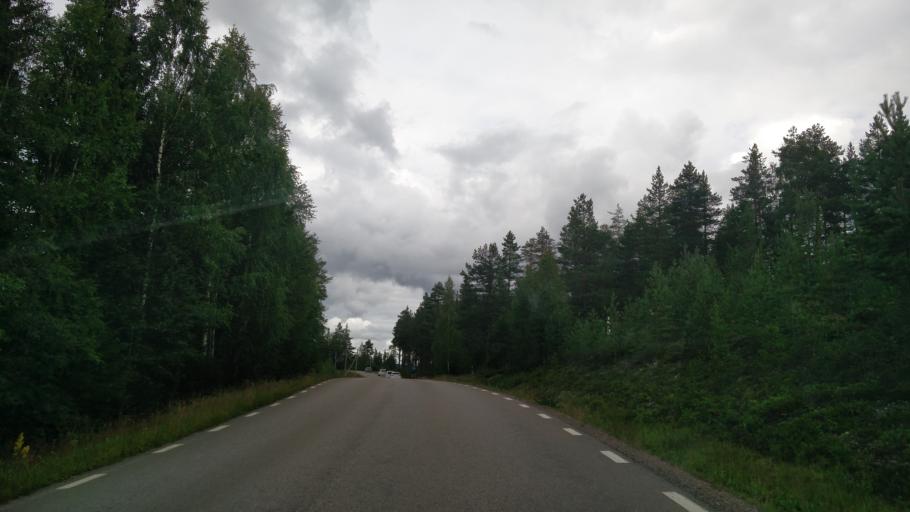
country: NO
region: Hedmark
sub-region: Trysil
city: Innbygda
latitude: 61.1604
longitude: 12.8218
